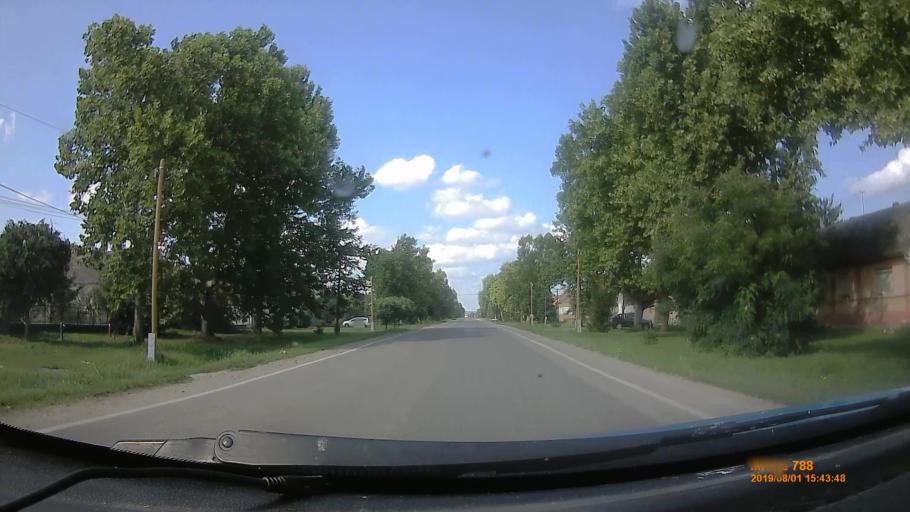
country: HU
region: Baranya
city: Szentlorinc
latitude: 46.0026
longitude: 17.9707
